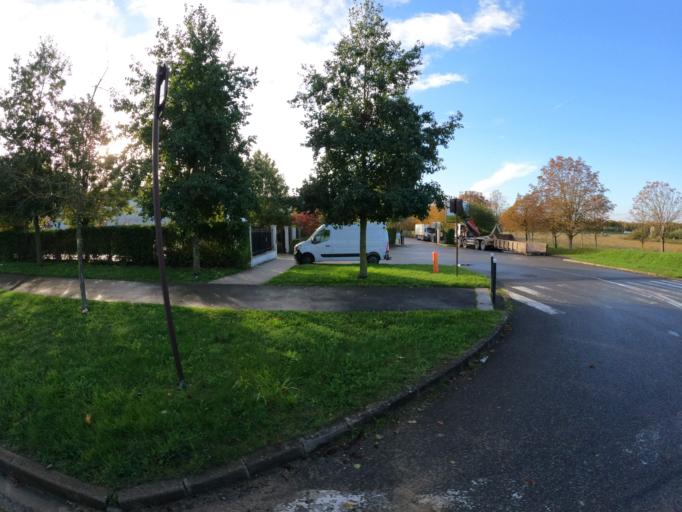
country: FR
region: Ile-de-France
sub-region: Departement de Seine-et-Marne
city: Bussy-Saint-Georges
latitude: 48.8326
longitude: 2.7037
